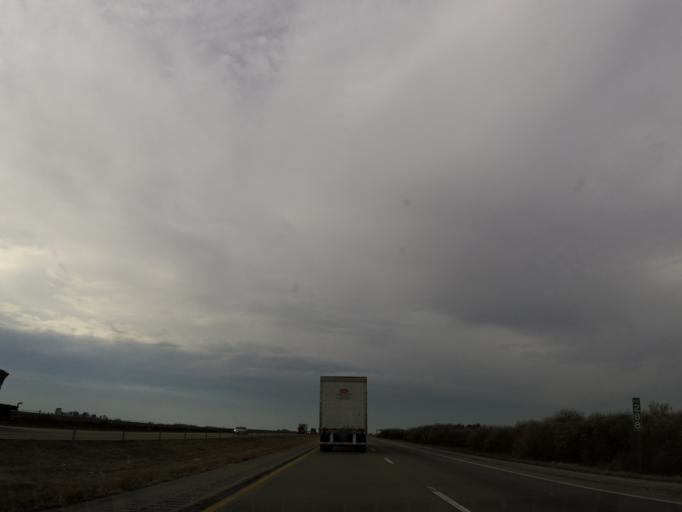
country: US
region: Iowa
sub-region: Scott County
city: Walcott
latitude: 41.6037
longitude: -90.7145
